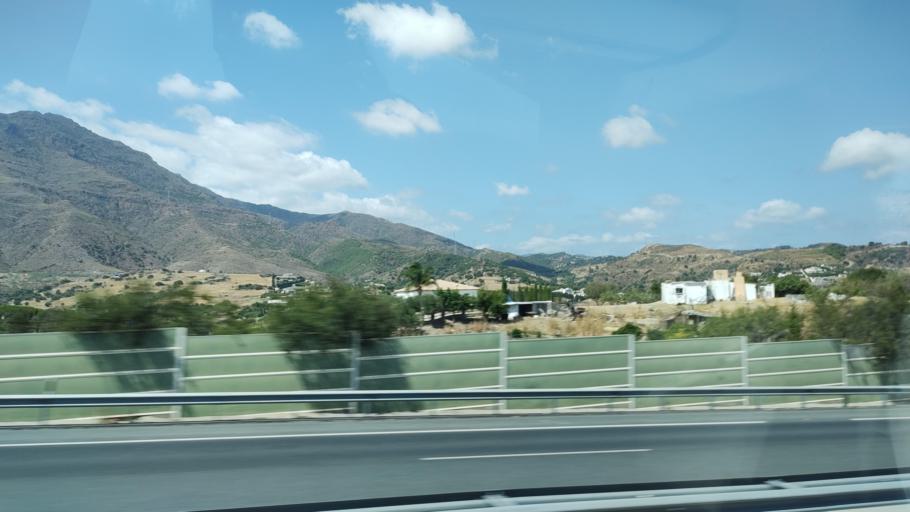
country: ES
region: Andalusia
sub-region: Provincia de Malaga
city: Estepona
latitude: 36.4326
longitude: -5.1890
